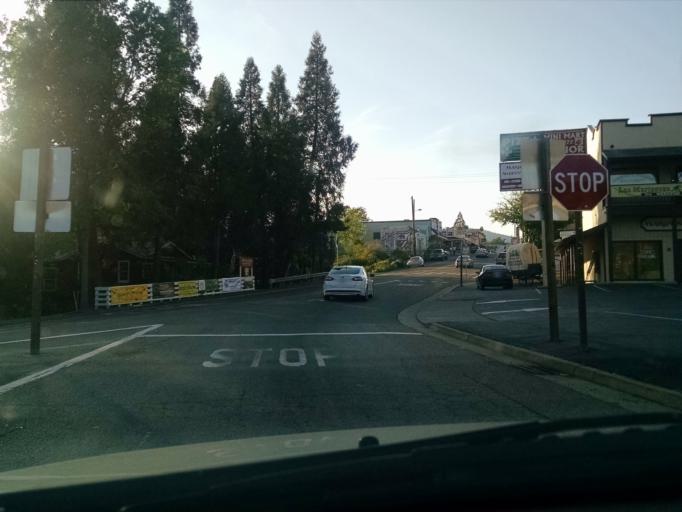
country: US
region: California
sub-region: Mariposa County
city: Mariposa
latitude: 37.4833
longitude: -119.9637
